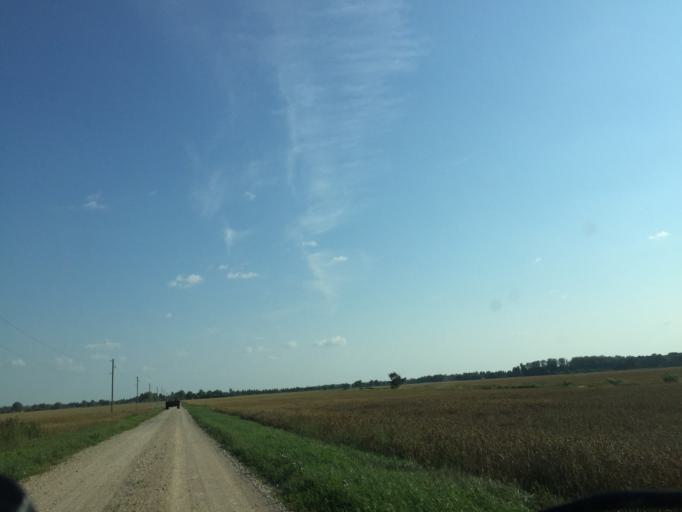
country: LV
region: Jelgava
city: Jelgava
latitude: 56.4641
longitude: 23.6803
